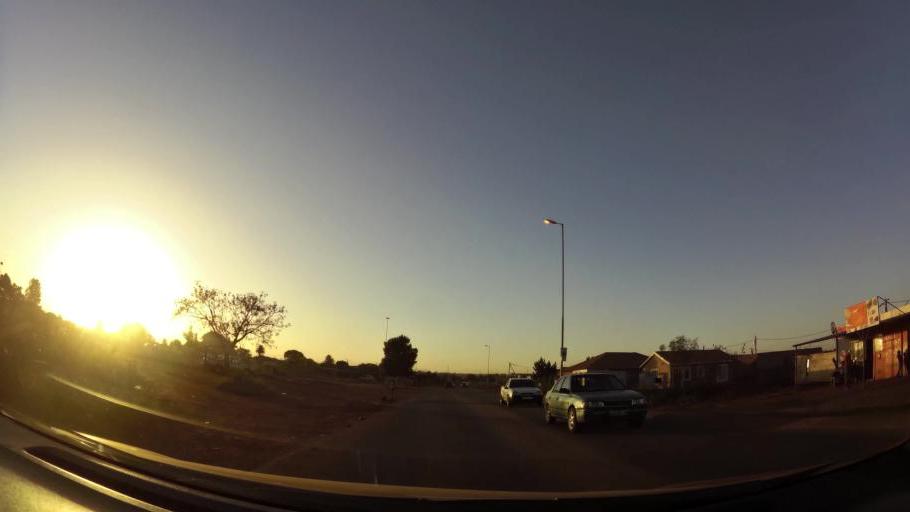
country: ZA
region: Gauteng
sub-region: City of Tshwane Metropolitan Municipality
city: Mabopane
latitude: -25.5904
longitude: 28.0904
